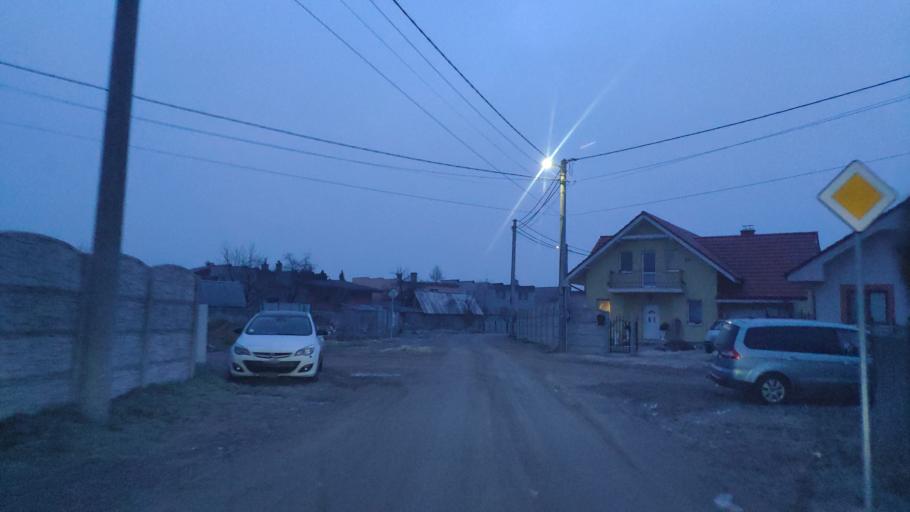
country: SK
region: Kosicky
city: Kosice
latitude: 48.6124
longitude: 21.3305
